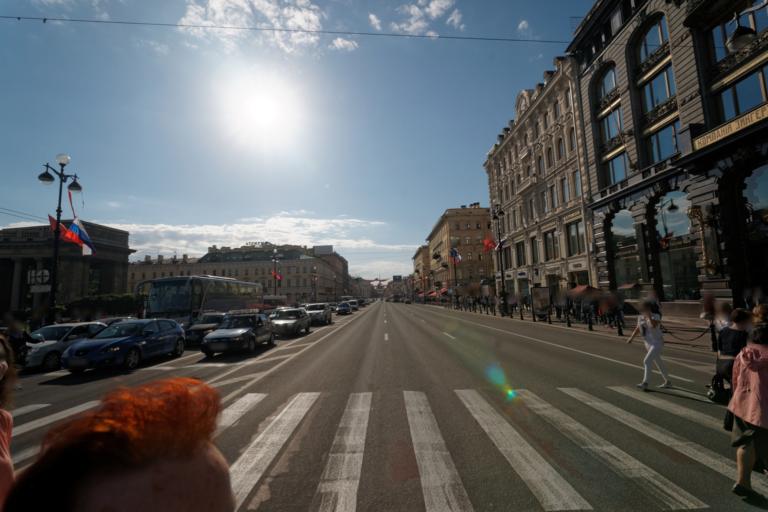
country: RU
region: St.-Petersburg
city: Saint Petersburg
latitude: 59.9354
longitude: 30.3260
